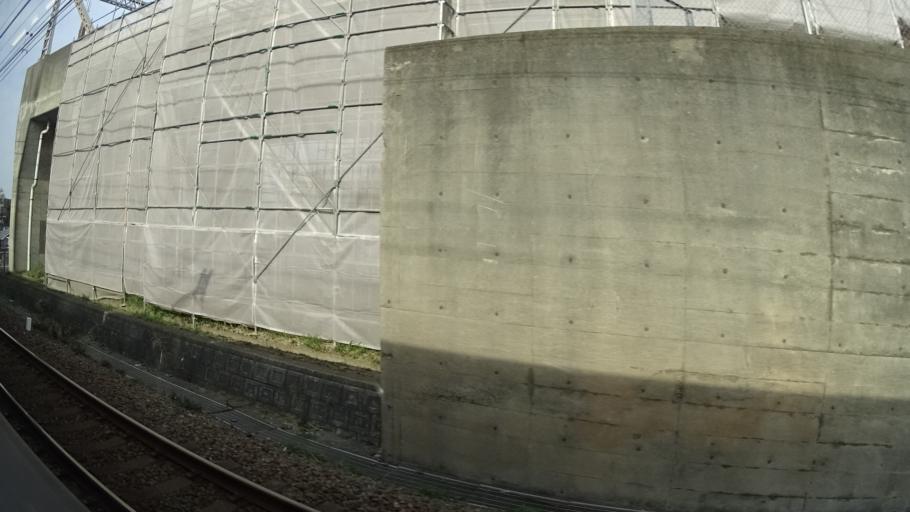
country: JP
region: Kanagawa
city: Zama
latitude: 35.4630
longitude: 139.4100
